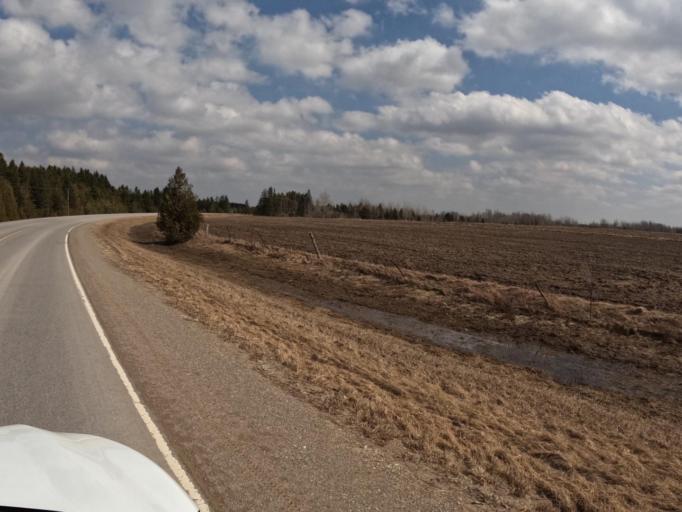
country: CA
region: Ontario
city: Shelburne
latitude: 44.0016
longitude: -80.2494
